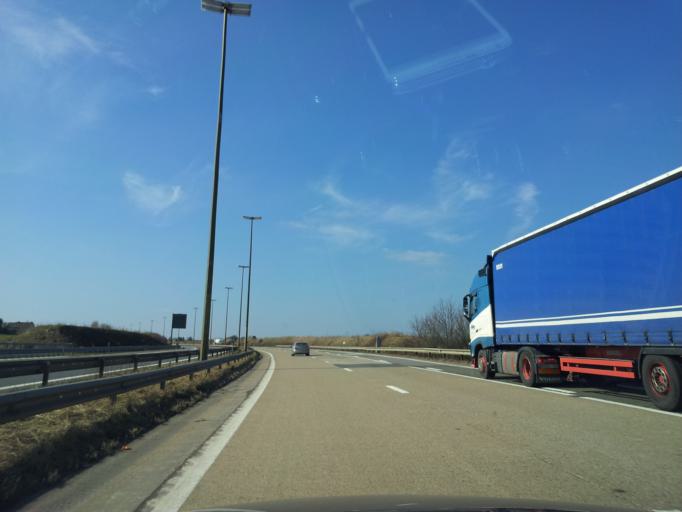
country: BE
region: Wallonia
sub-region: Province de Liege
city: Jalhay
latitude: 50.5286
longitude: 5.9154
